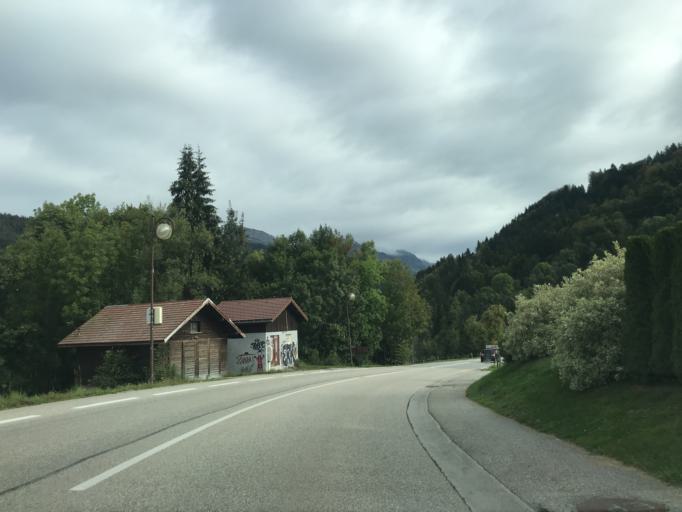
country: FR
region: Rhone-Alpes
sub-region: Departement de la Haute-Savoie
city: Saint-Jean-de-Sixt
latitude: 45.9248
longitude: 6.4095
